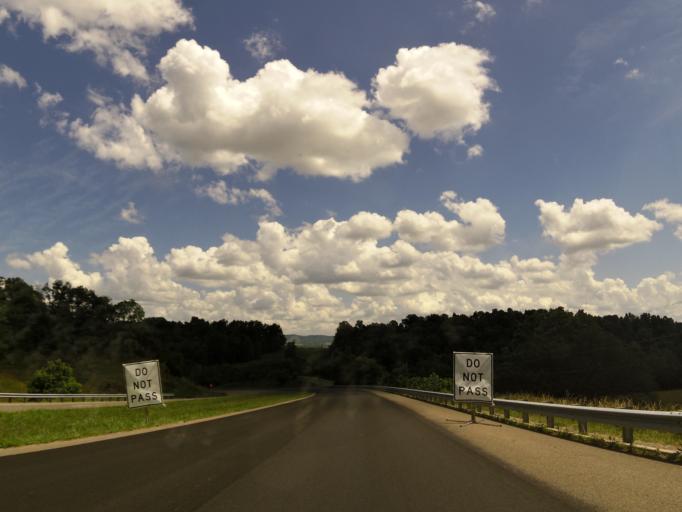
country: US
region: Virginia
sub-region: Lee County
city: Jonesville
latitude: 36.6759
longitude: -83.2125
